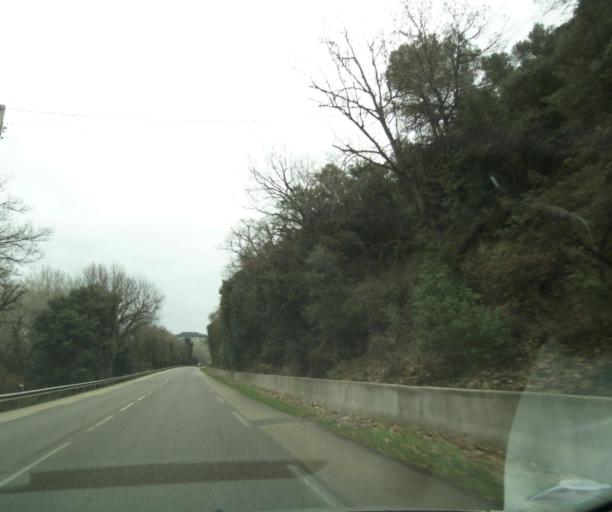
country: FR
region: Provence-Alpes-Cote d'Azur
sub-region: Departement des Bouches-du-Rhone
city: Jouques
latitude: 43.6557
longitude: 5.6225
